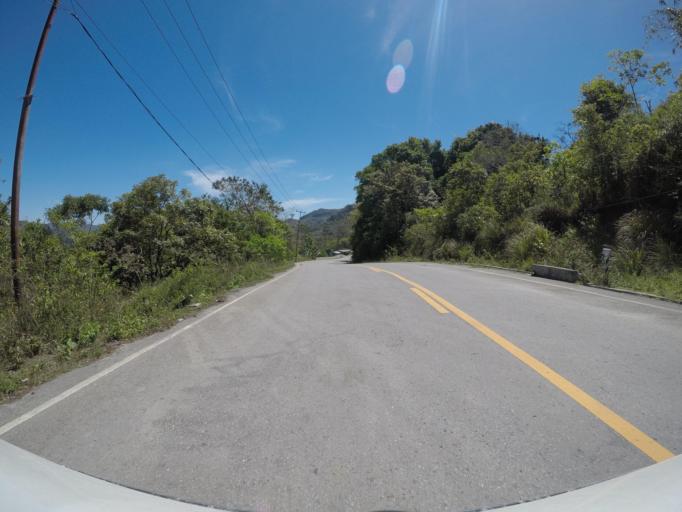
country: TL
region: Manatuto
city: Manatuto
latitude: -8.7992
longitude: 125.9697
